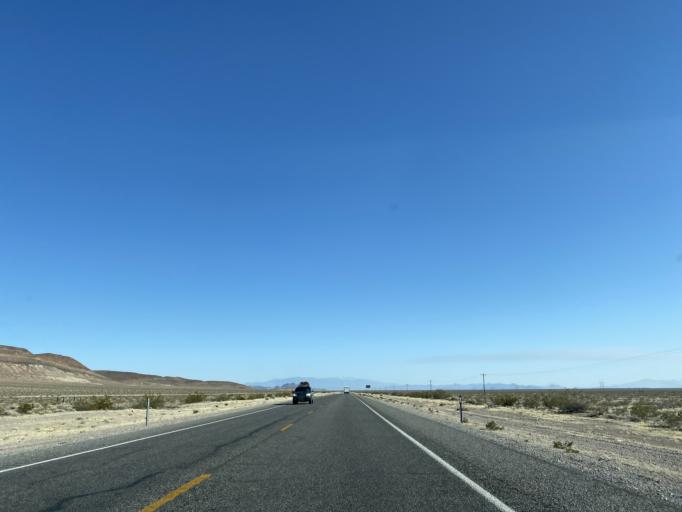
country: US
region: Nevada
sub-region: Nye County
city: Beatty
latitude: 36.6890
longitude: -116.5598
